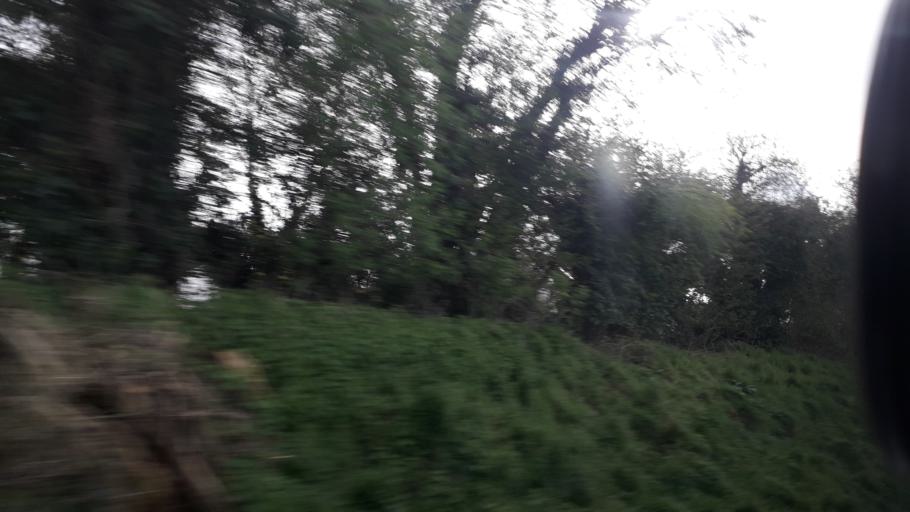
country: IE
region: Leinster
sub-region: An Mhi
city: Longwood
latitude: 53.4180
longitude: -6.8928
